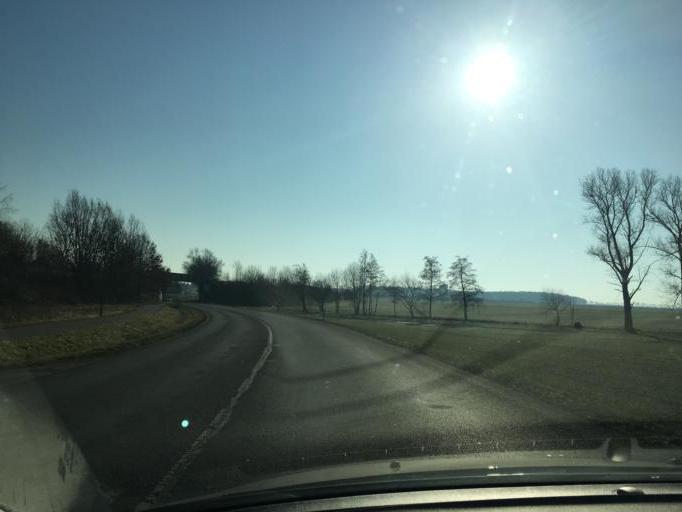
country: DE
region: Saxony
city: Grossposna
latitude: 51.2732
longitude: 12.4767
